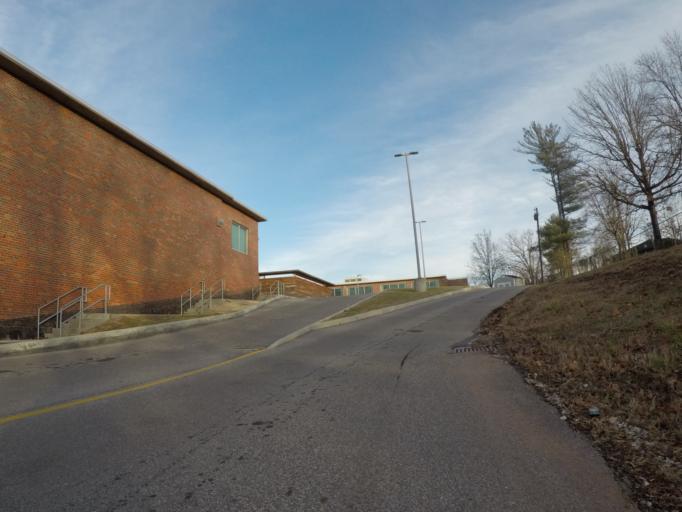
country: US
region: West Virginia
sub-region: Cabell County
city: Huntington
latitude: 38.4070
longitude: -82.3919
